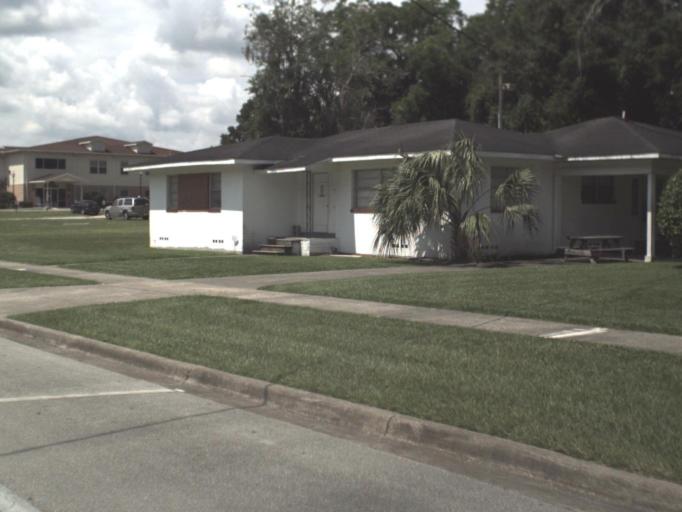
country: US
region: Florida
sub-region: Alachua County
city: Alachua
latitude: 29.7899
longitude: -82.4943
